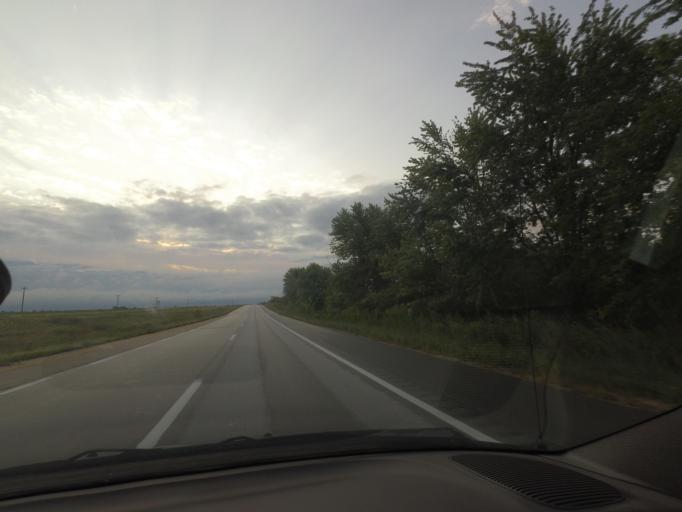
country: US
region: Missouri
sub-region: Shelby County
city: Shelbina
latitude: 39.7036
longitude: -92.0822
